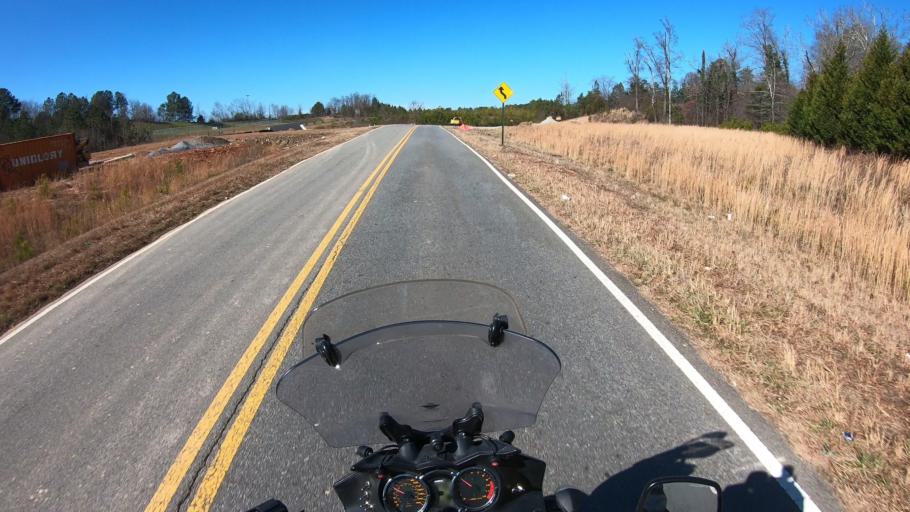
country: US
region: Georgia
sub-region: Bartow County
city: Rydal
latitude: 34.2756
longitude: -84.8056
